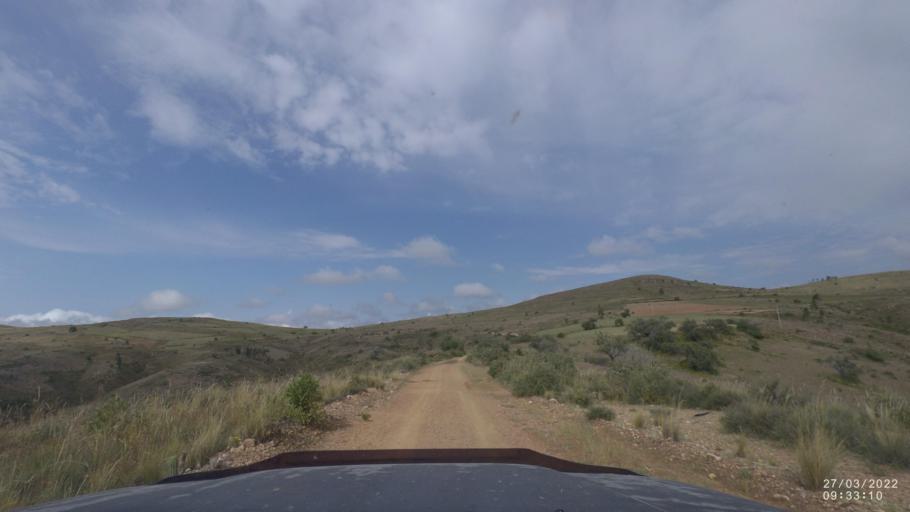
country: BO
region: Cochabamba
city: Cliza
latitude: -17.7391
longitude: -65.8878
